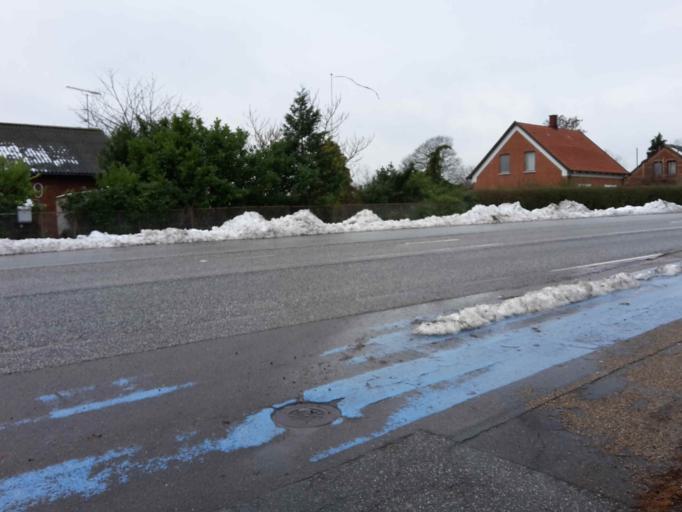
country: DK
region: Capital Region
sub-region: Allerod Kommune
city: Blovstrod
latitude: 55.8638
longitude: 12.3875
